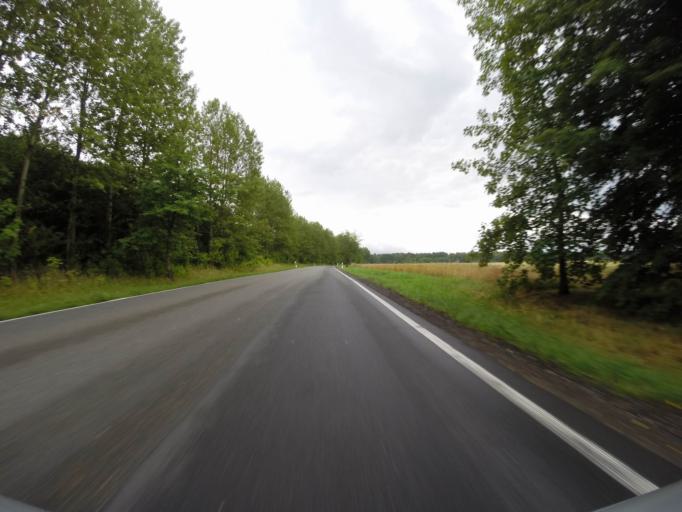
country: DE
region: Thuringia
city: Hainspitz
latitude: 50.9405
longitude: 11.8272
